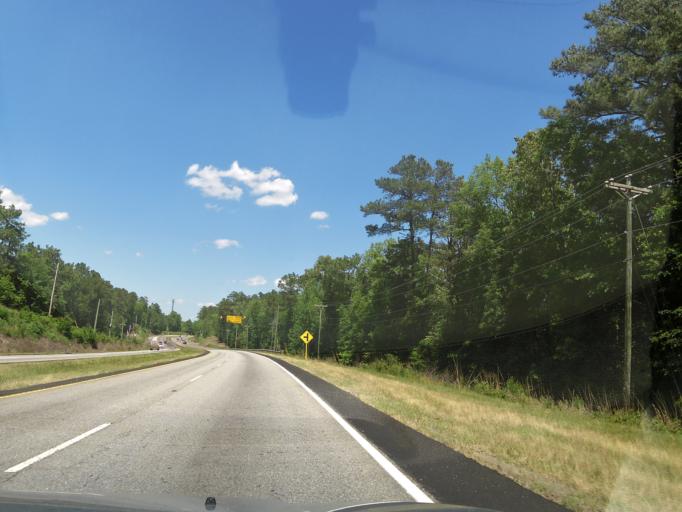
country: US
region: South Carolina
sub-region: Aiken County
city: Warrenville
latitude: 33.5459
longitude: -81.8226
